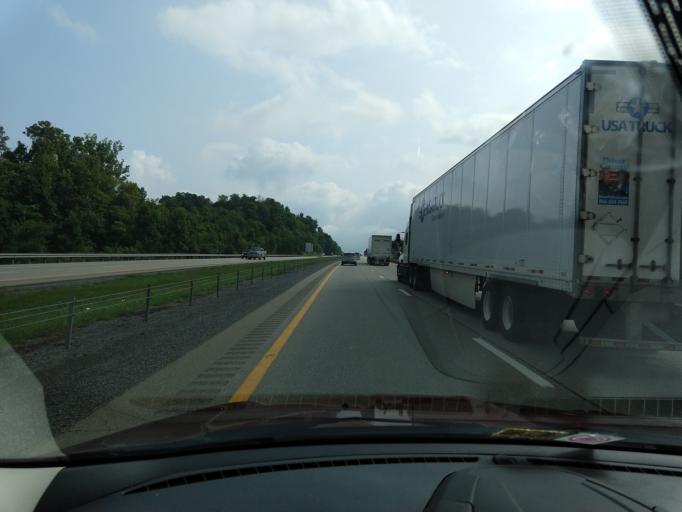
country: US
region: West Virginia
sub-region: Marion County
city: Pleasant Valley
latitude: 39.4466
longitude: -80.1617
